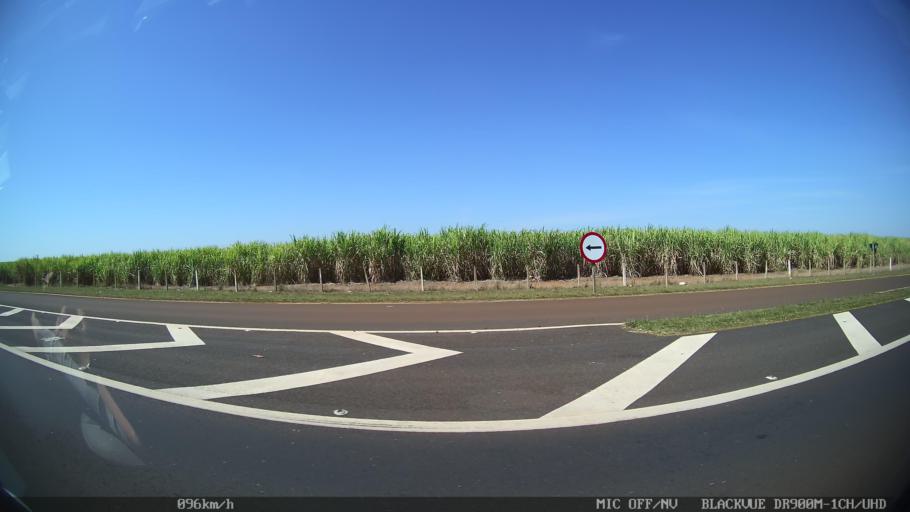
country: BR
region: Sao Paulo
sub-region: Batatais
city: Batatais
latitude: -20.8273
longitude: -47.5952
